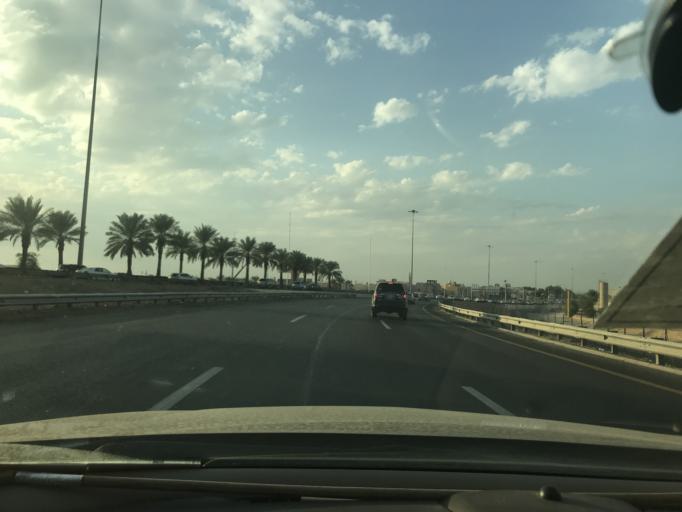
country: SA
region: Ar Riyad
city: Riyadh
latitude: 24.7394
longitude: 46.5891
